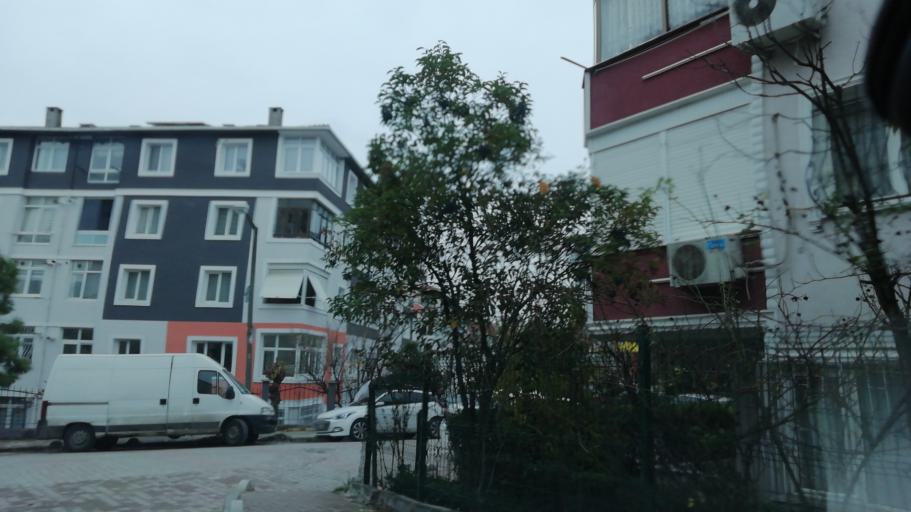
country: TR
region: Istanbul
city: Mahmutbey
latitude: 41.0173
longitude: 28.8232
